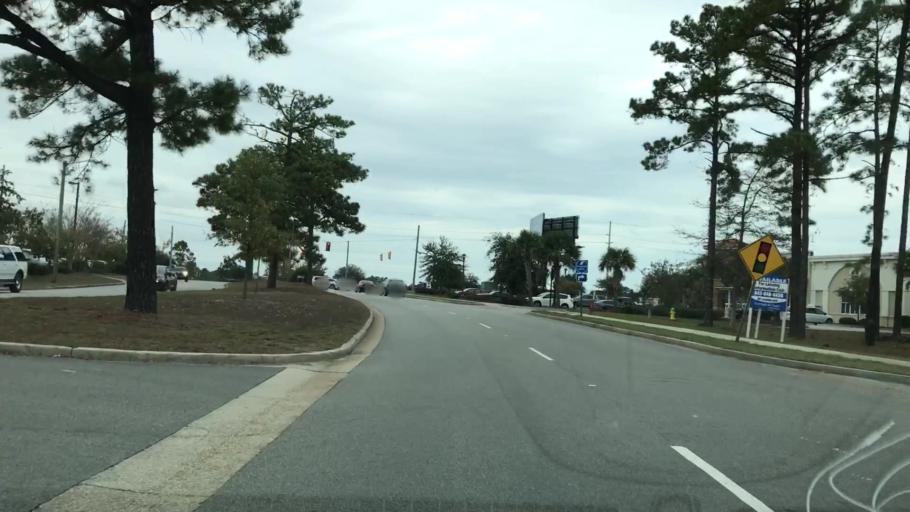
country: US
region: South Carolina
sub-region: Horry County
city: Myrtle Beach
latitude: 33.7602
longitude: -78.8164
